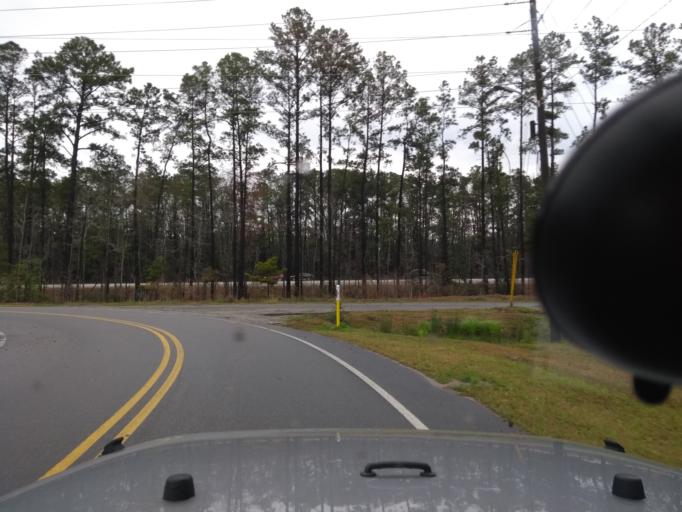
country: US
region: Georgia
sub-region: Chatham County
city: Garden City
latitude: 32.0684
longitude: -81.1658
